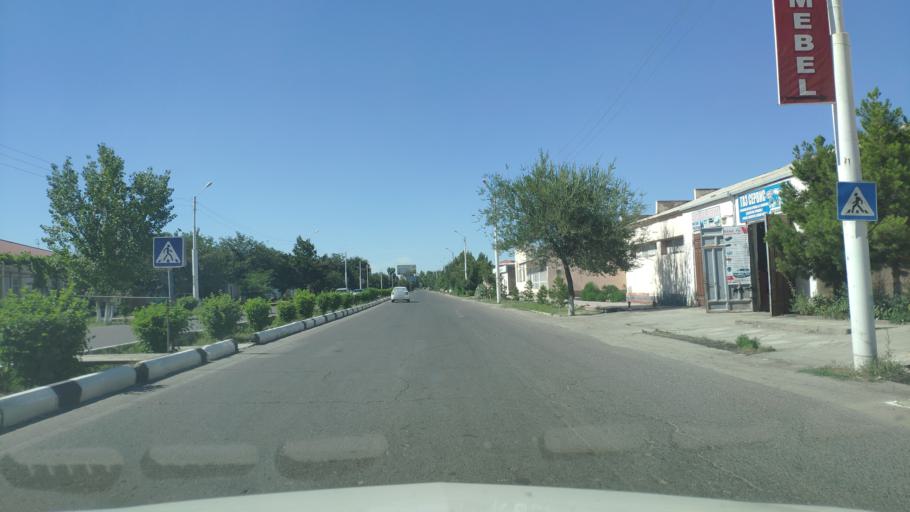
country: UZ
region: Bukhara
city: Bukhara
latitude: 39.7864
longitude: 64.4201
